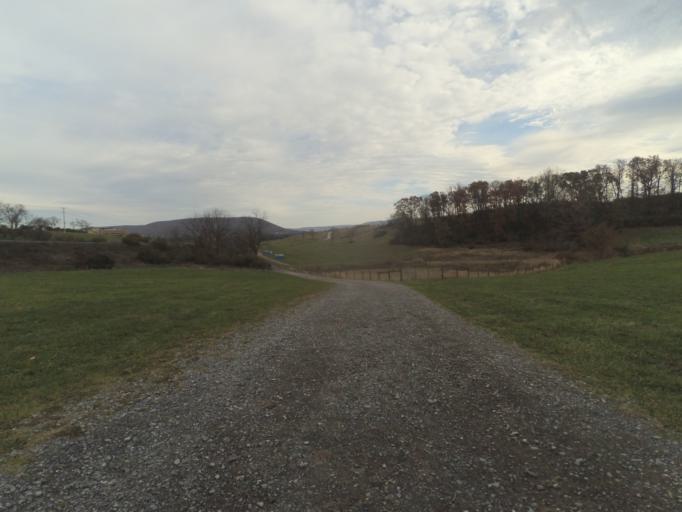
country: US
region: Pennsylvania
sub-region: Centre County
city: Houserville
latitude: 40.8175
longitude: -77.8508
